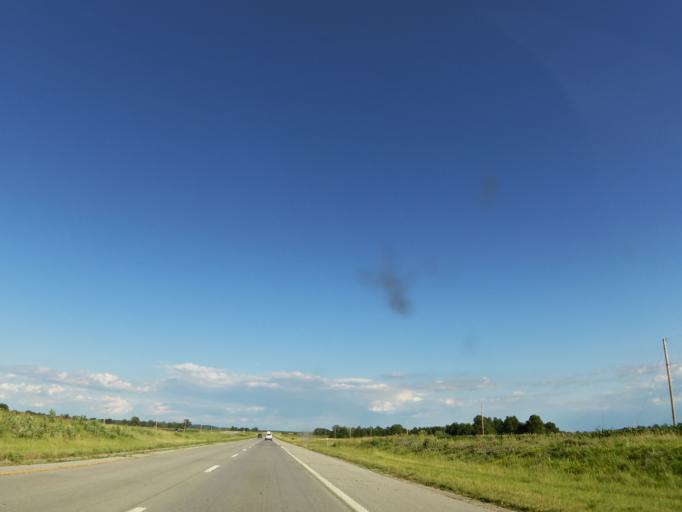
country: US
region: Missouri
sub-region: Pike County
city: Bowling Green
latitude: 39.3119
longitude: -91.1352
